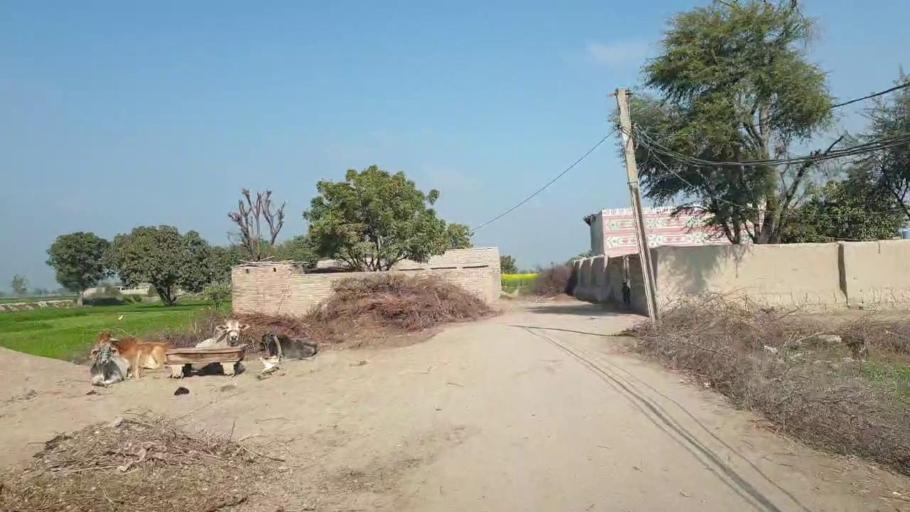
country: PK
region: Sindh
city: Shahdadpur
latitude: 26.0155
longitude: 68.5910
